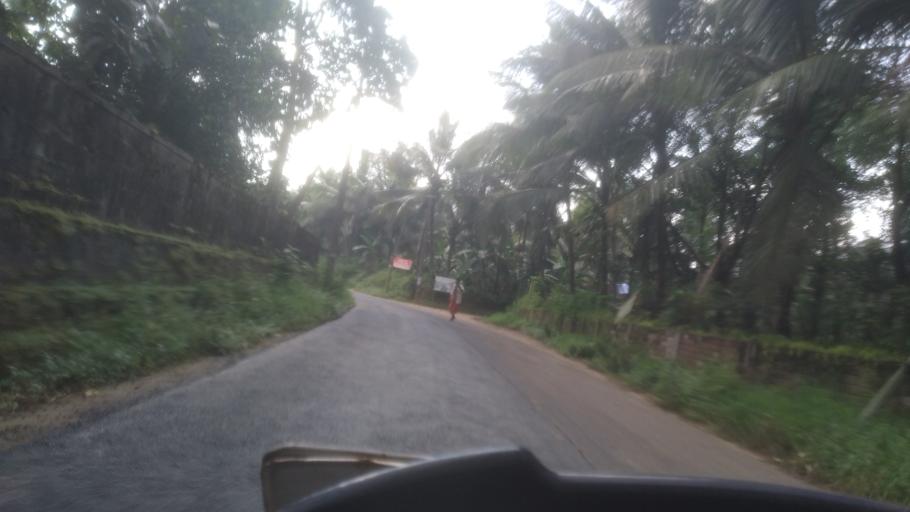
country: IN
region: Kerala
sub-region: Ernakulam
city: Kotamangalam
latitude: 10.0021
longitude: 76.7340
